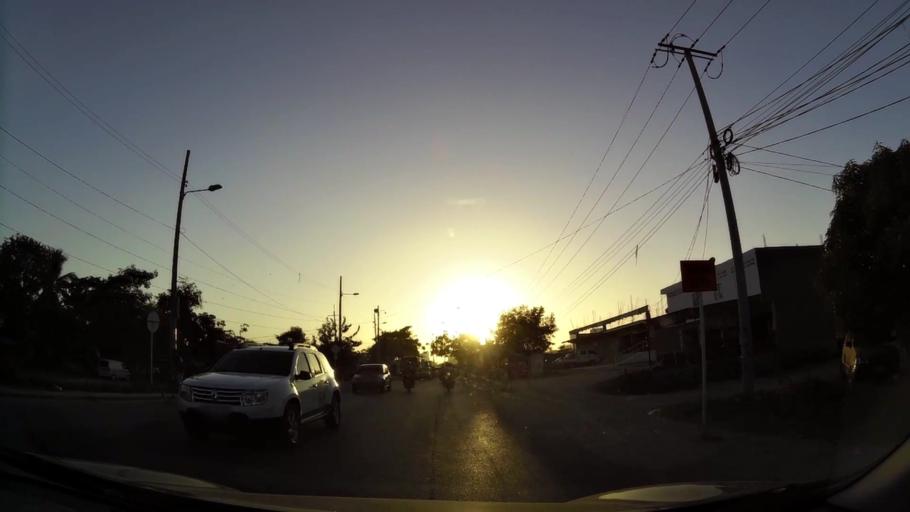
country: CO
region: Bolivar
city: Cartagena
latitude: 10.3987
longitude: -75.4703
